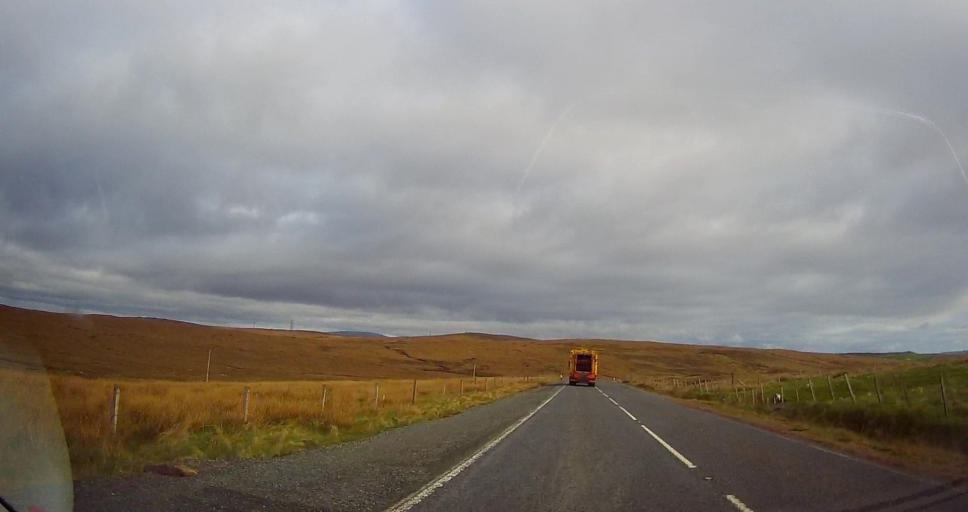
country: GB
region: Scotland
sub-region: Shetland Islands
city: Lerwick
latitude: 60.4483
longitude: -1.2109
